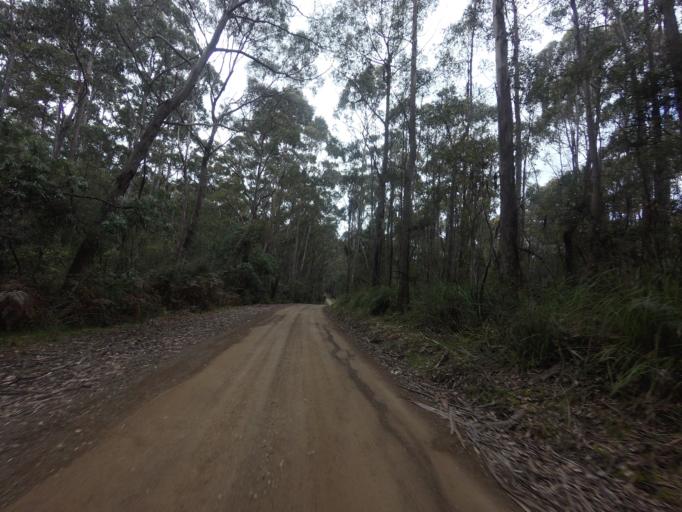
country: AU
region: Tasmania
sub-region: Huon Valley
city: Geeveston
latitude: -43.4241
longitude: 147.0076
